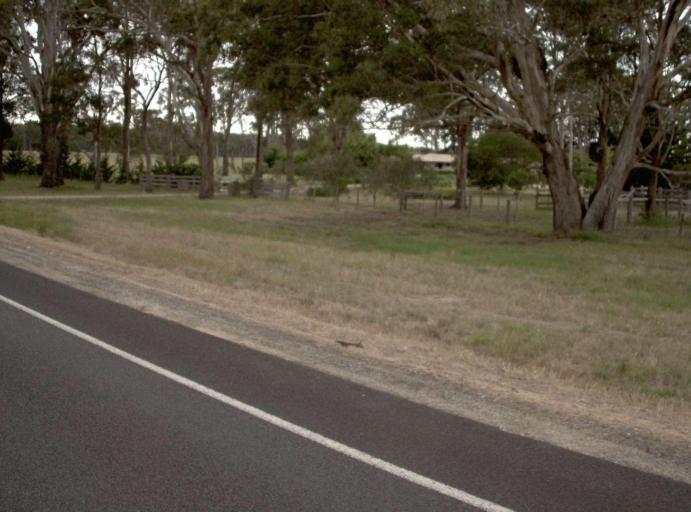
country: AU
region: Victoria
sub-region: Wellington
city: Sale
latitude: -38.4697
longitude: 146.9297
